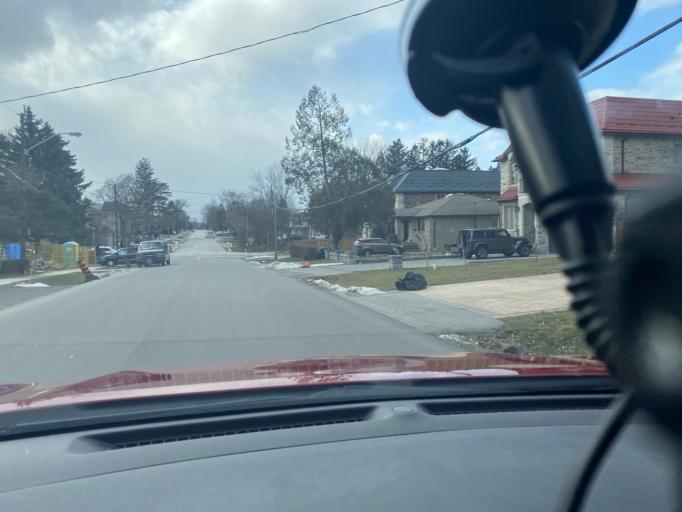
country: CA
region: Ontario
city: Scarborough
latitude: 43.7955
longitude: -79.1673
